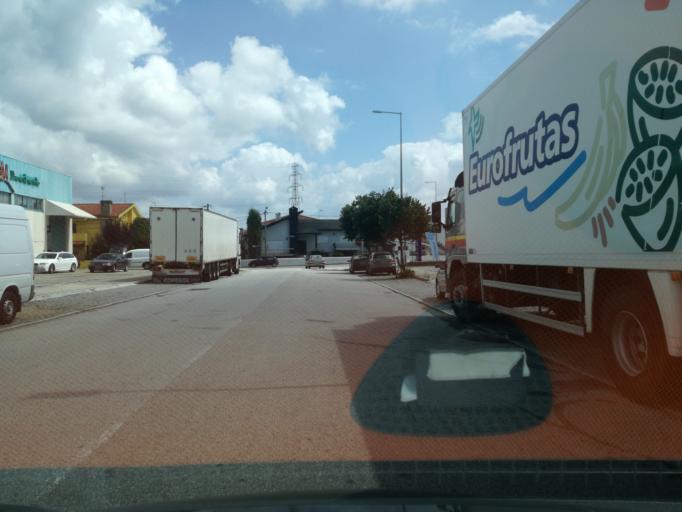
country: PT
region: Porto
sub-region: Valongo
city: Alfena
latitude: 41.2344
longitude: -8.5364
